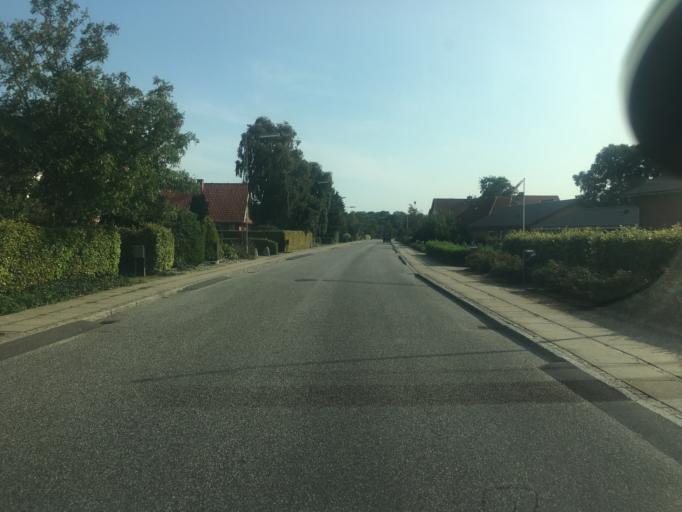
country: DK
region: South Denmark
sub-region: Tonder Kommune
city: Tonder
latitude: 54.9455
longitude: 8.8791
